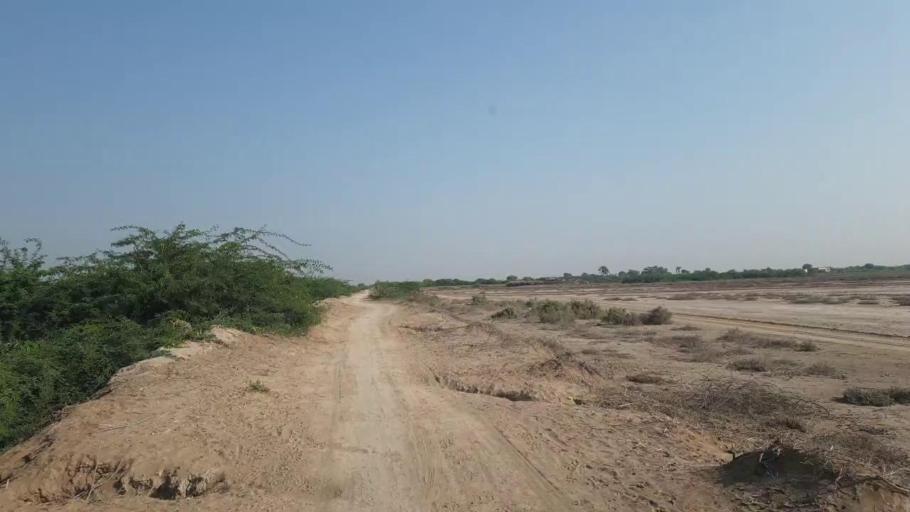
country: PK
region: Sindh
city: Badin
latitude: 24.4602
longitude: 68.7366
